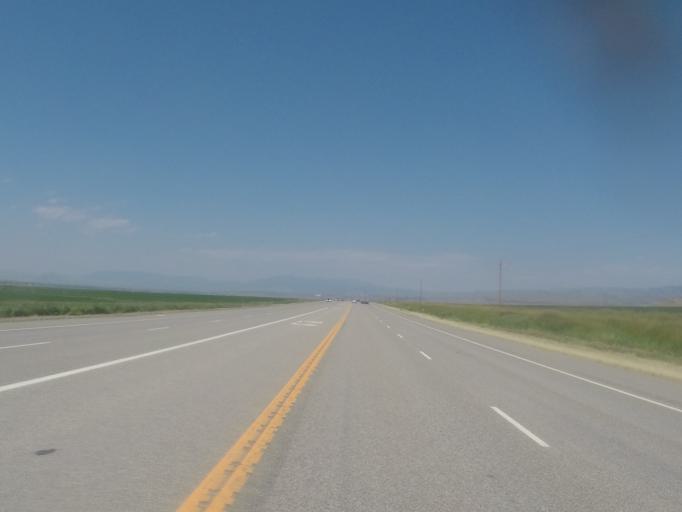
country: US
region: Montana
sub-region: Broadwater County
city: Townsend
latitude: 46.1079
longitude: -111.5102
